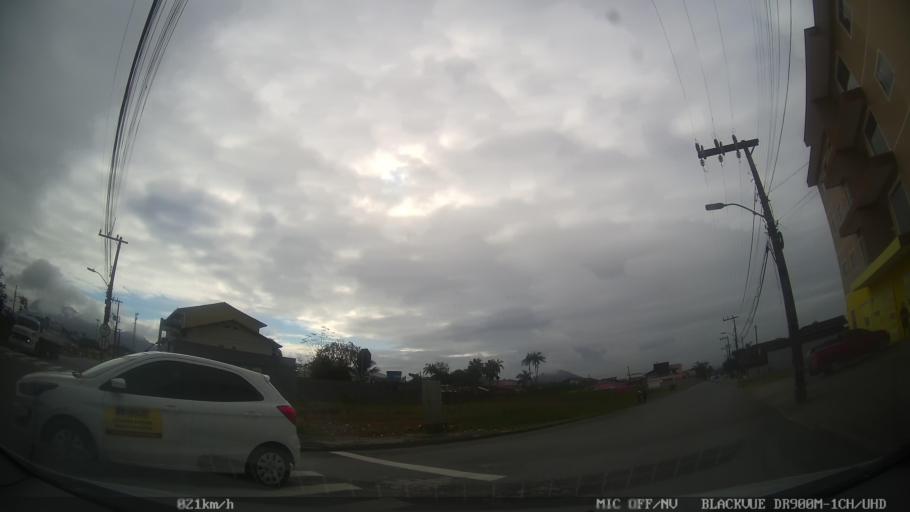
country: BR
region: Santa Catarina
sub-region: Joinville
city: Joinville
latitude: -26.0342
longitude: -48.8564
